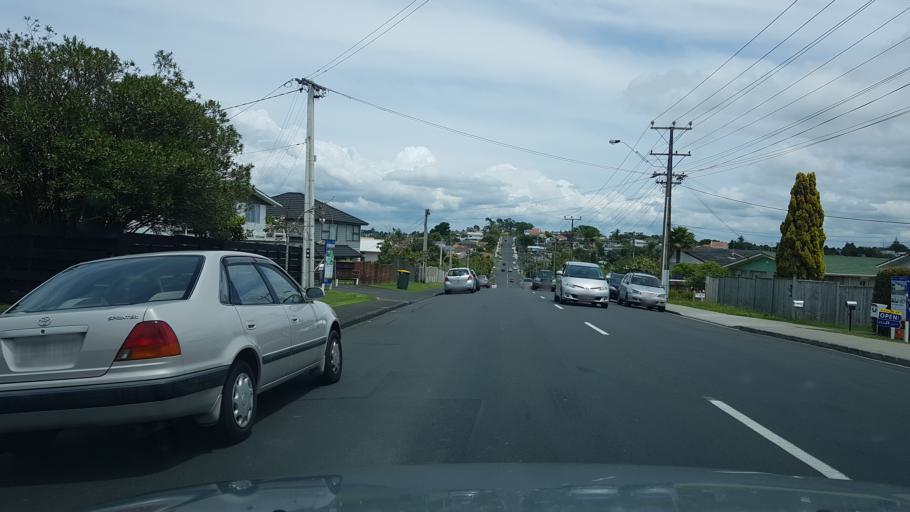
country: NZ
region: Auckland
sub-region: Auckland
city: North Shore
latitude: -36.8016
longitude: 174.7339
